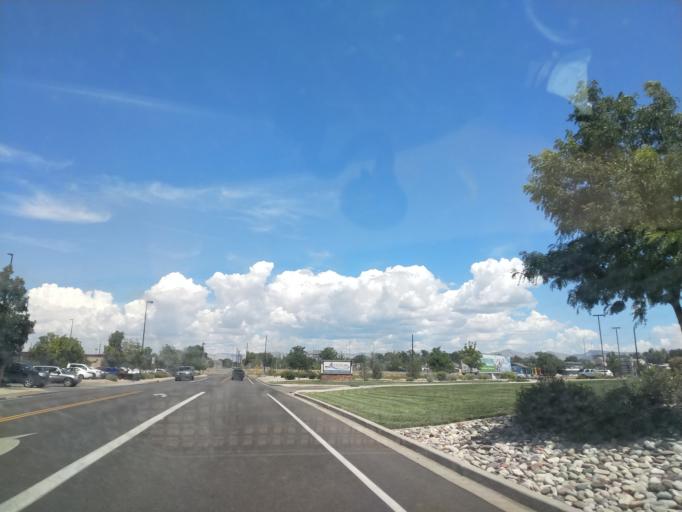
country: US
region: Colorado
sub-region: Mesa County
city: Grand Junction
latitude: 39.0764
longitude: -108.5802
